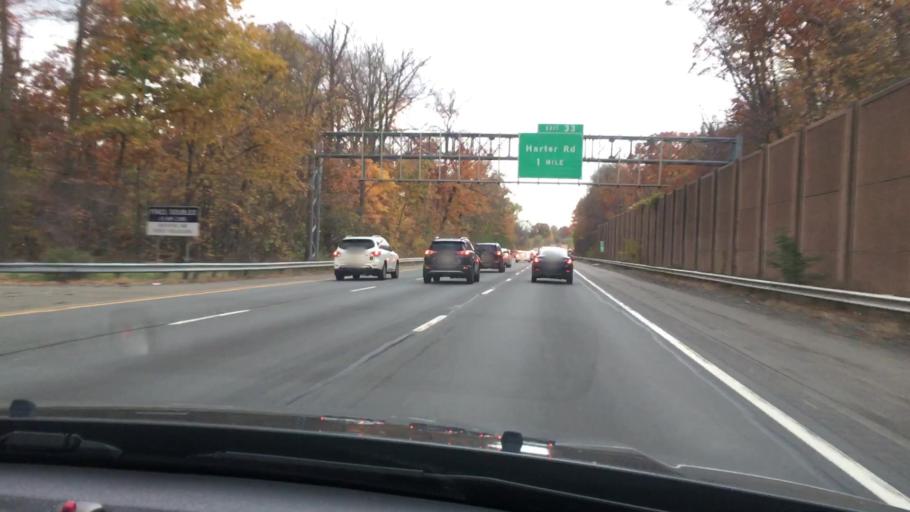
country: US
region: New Jersey
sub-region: Morris County
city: Morristown
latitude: 40.7789
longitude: -74.4753
